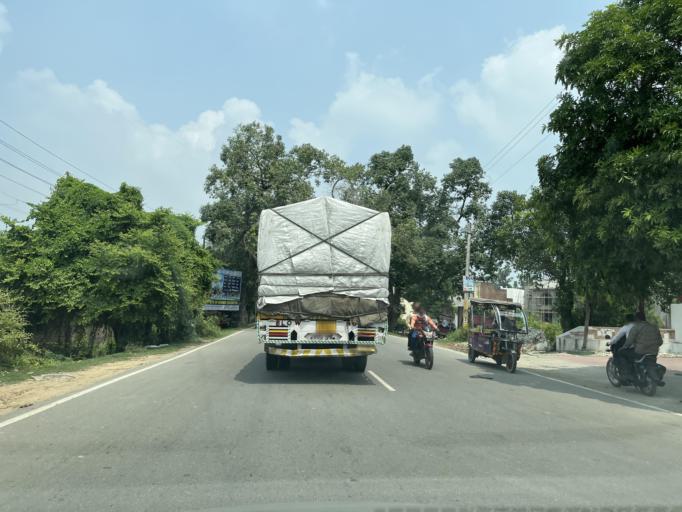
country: IN
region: Uttar Pradesh
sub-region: Bijnor
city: Najibabad
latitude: 29.5960
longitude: 78.3394
